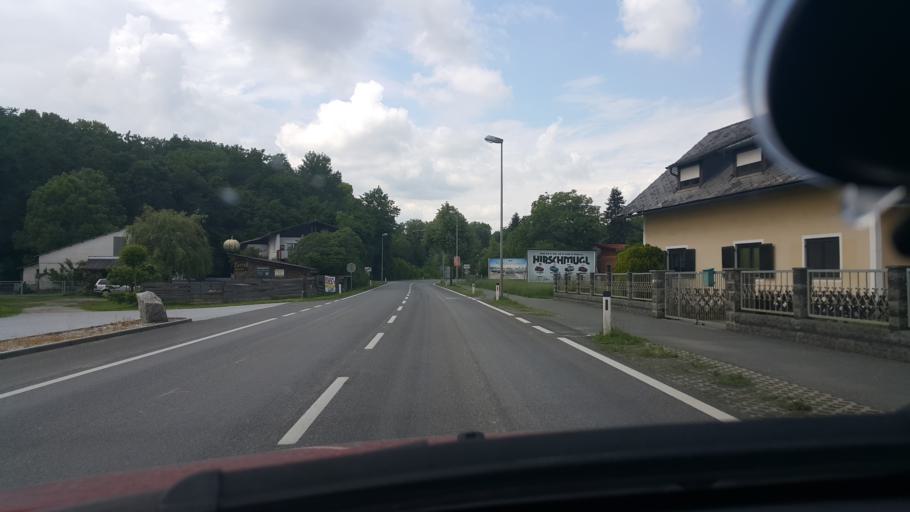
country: AT
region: Styria
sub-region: Politischer Bezirk Leibnitz
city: Weitendorf
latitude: 46.8892
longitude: 15.4816
